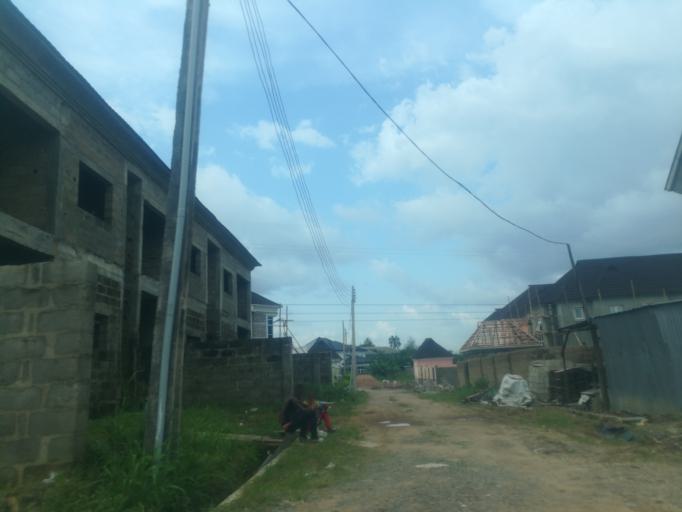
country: NG
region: Oyo
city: Ibadan
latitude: 7.3673
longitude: 3.8488
